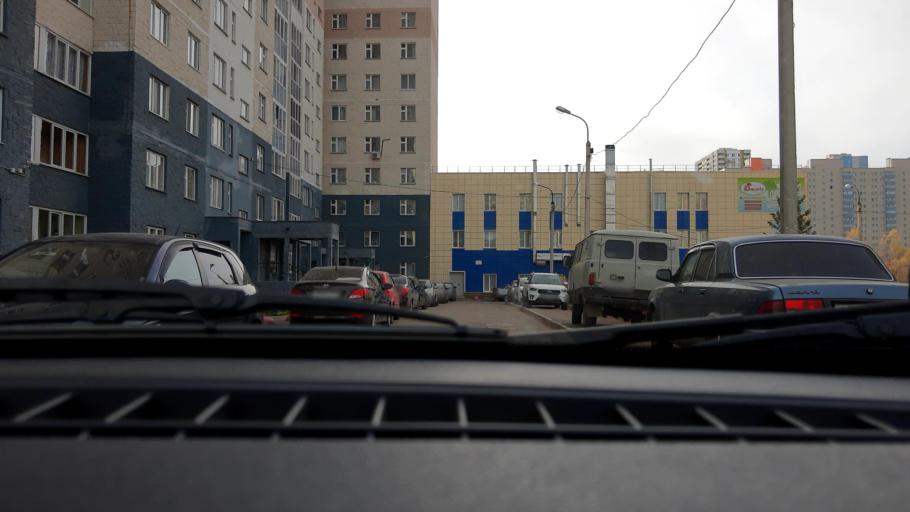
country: RU
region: Bashkortostan
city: Ufa
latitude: 54.7820
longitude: 56.1376
